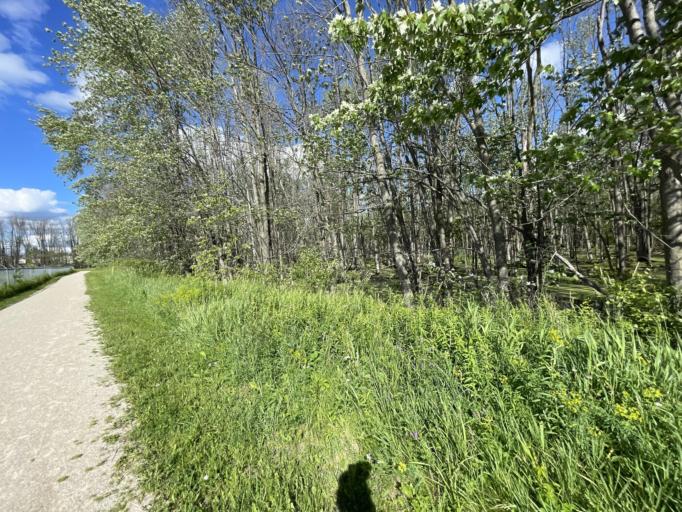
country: CA
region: Ontario
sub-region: Wellington County
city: Guelph
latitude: 43.5771
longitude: -80.2269
